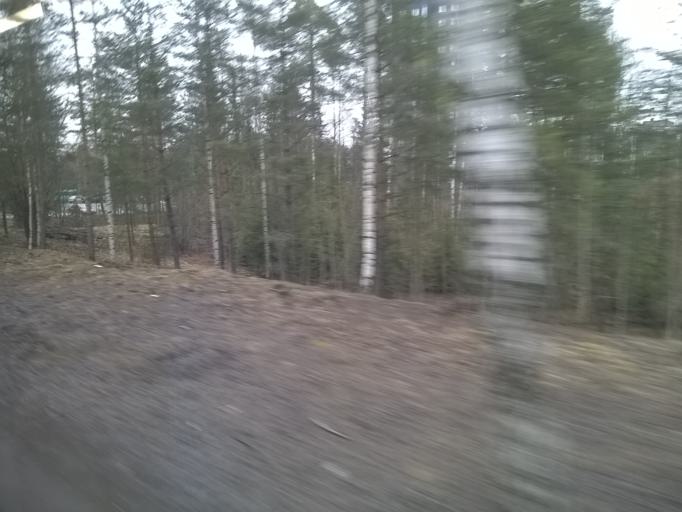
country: FI
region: Pirkanmaa
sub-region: Tampere
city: Tampere
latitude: 61.4567
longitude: 23.8459
